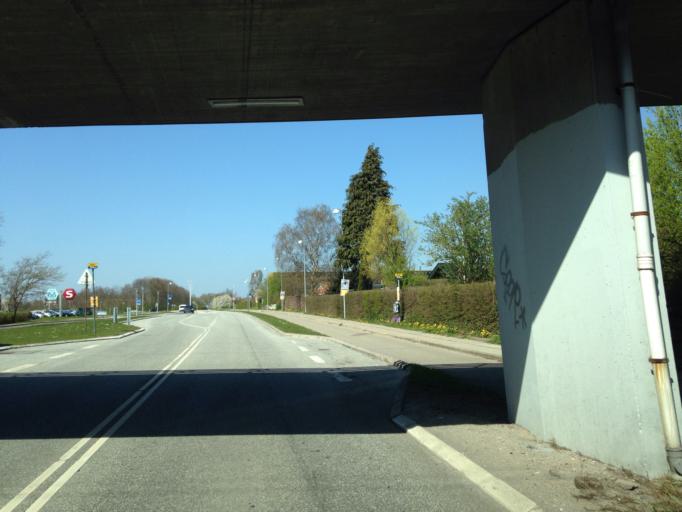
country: DK
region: Zealand
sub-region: Greve Kommune
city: Greve
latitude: 55.5825
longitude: 12.2987
